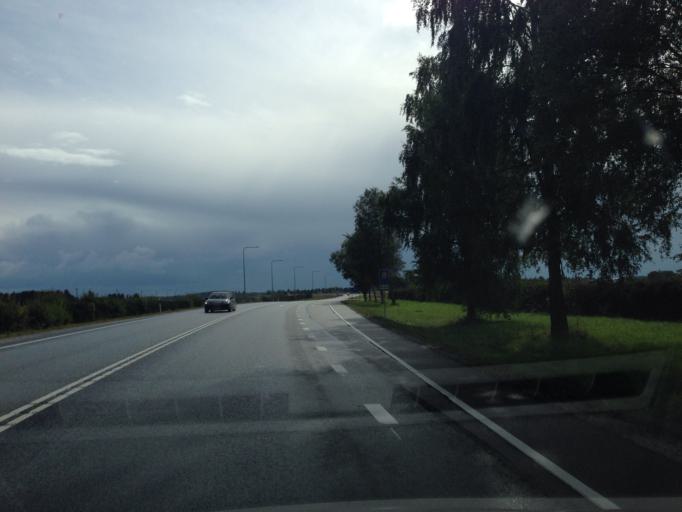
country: EE
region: Jaervamaa
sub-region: Paide linn
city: Paide
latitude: 58.9422
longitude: 25.6123
